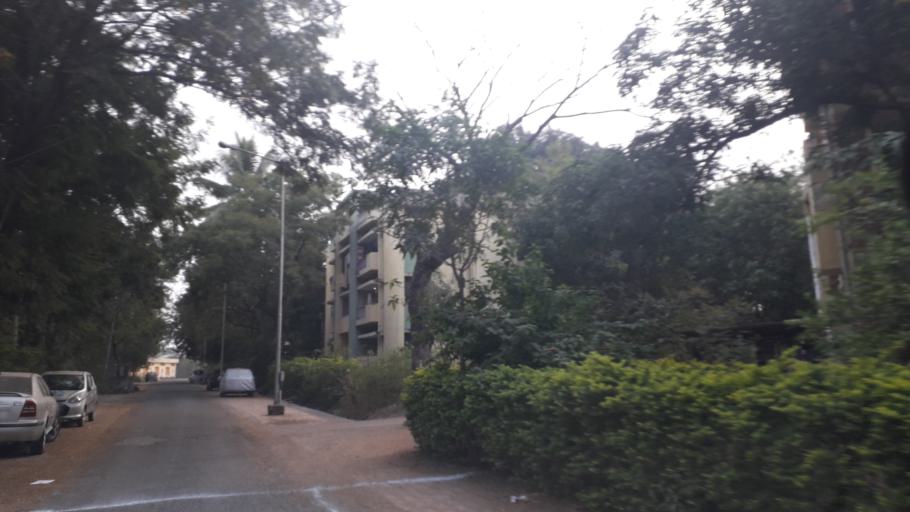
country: IN
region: Telangana
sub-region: Rangareddi
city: Singapur
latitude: 17.4671
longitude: 78.1647
